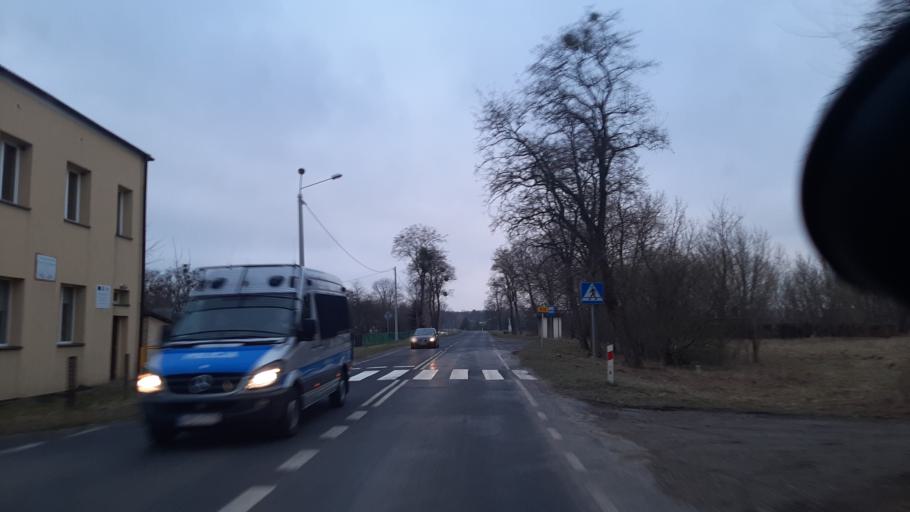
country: PL
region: Lublin Voivodeship
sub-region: Powiat parczewski
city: Debowa Kloda
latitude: 51.6383
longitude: 23.0357
